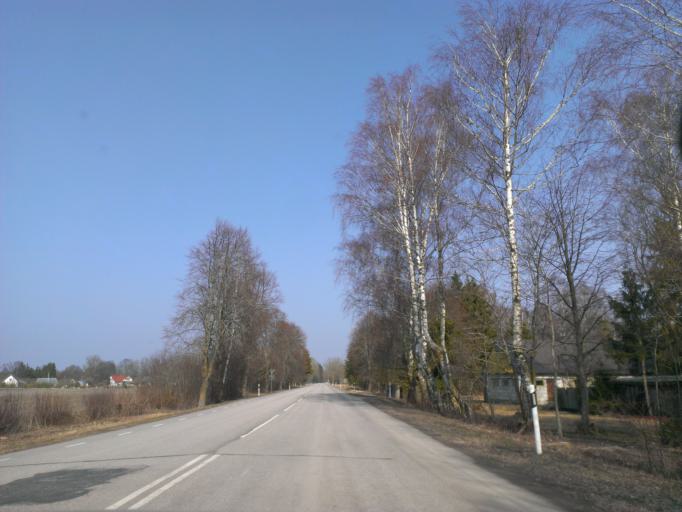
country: EE
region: Saare
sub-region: Orissaare vald
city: Orissaare
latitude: 58.5277
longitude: 23.0376
